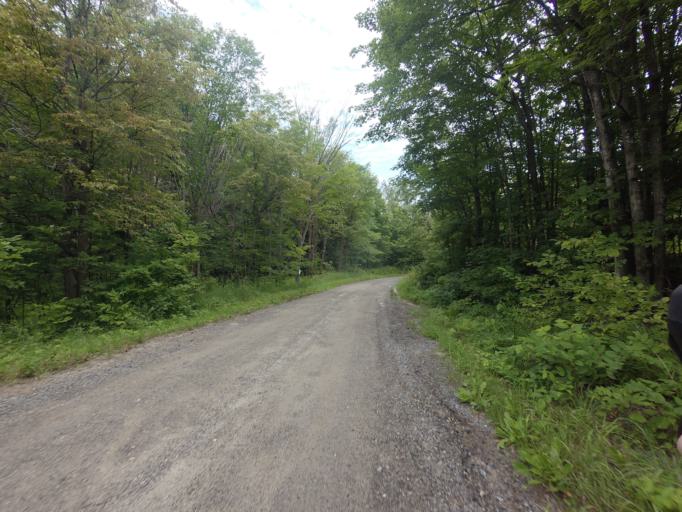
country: CA
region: Ontario
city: Perth
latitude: 44.6994
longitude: -76.6469
